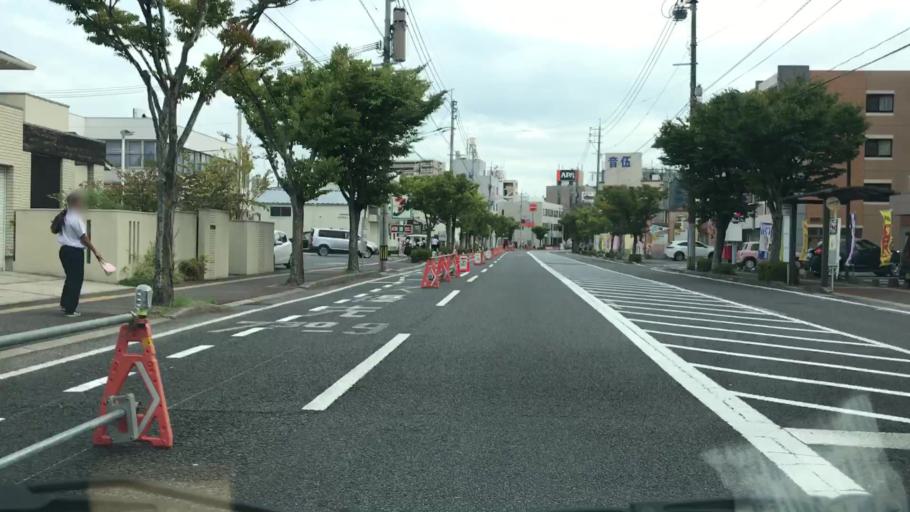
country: JP
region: Saga Prefecture
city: Saga-shi
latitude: 33.2703
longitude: 130.2955
